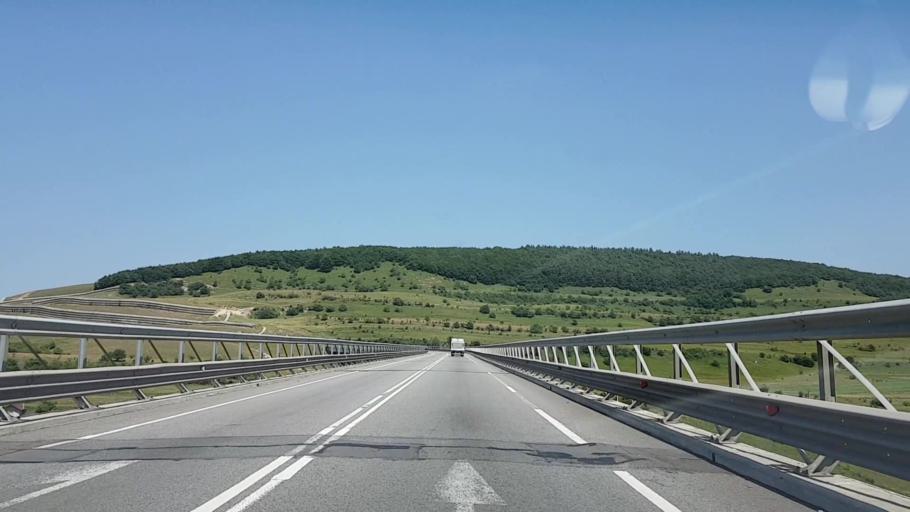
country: RO
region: Cluj
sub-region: Comuna Feleacu
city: Feleacu
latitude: 46.6894
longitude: 23.6318
